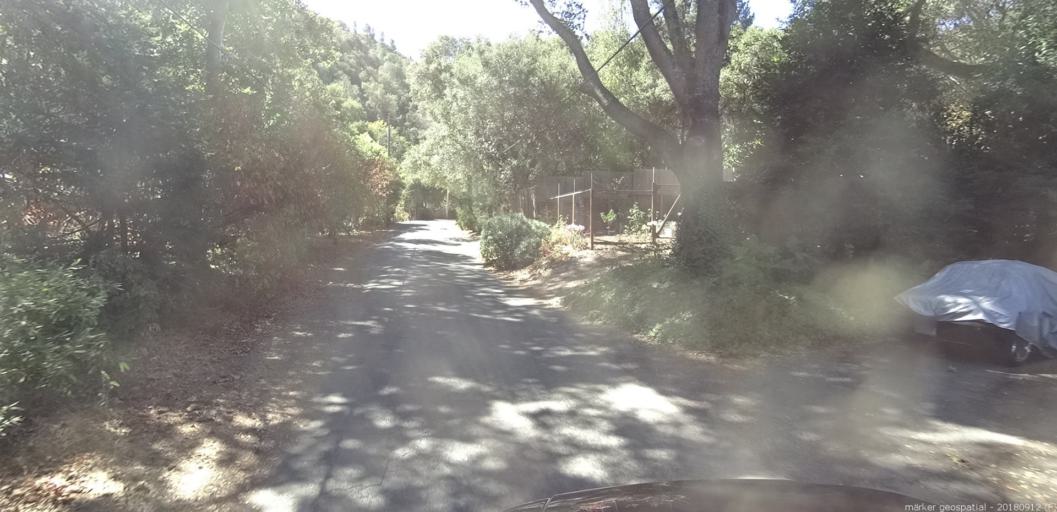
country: US
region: California
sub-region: Monterey County
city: Carmel Valley Village
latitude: 36.4647
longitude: -121.7241
